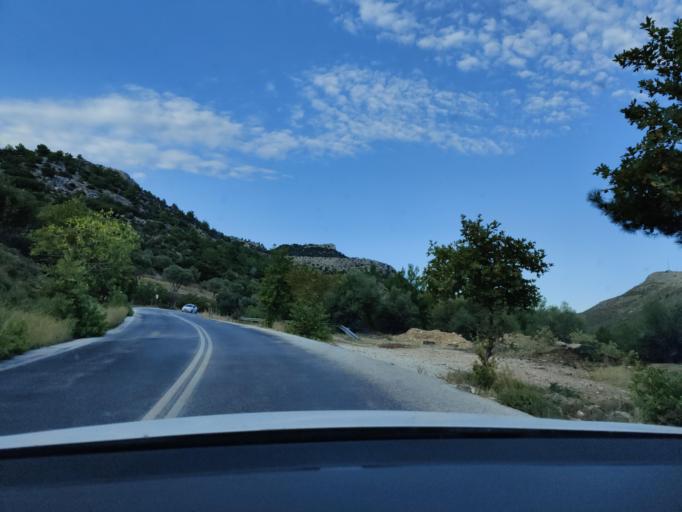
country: GR
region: East Macedonia and Thrace
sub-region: Nomos Kavalas
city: Limenaria
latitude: 40.6162
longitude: 24.6401
